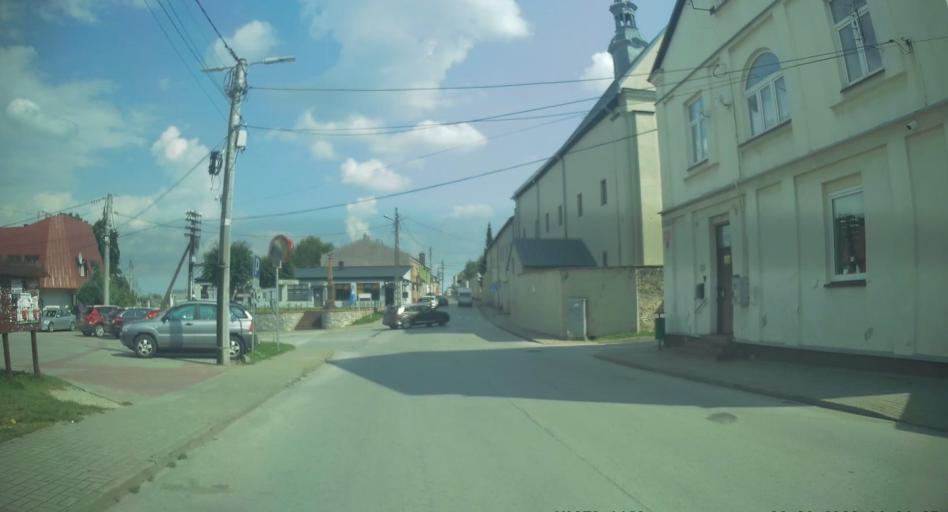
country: PL
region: Swietokrzyskie
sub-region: Powiat kielecki
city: Checiny
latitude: 50.8014
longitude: 20.4585
